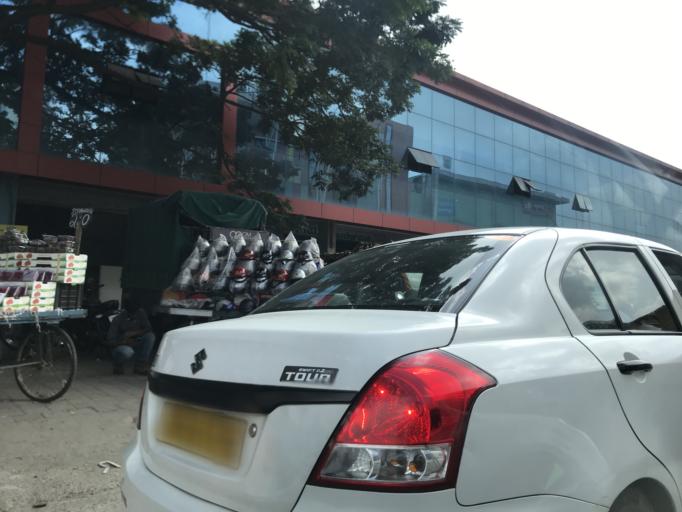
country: IN
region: Karnataka
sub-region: Bangalore Urban
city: Bangalore
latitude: 12.9659
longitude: 77.5627
